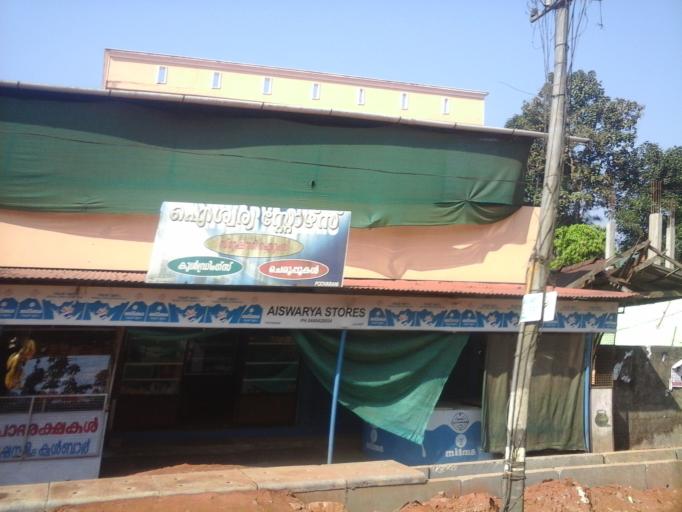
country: IN
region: Kerala
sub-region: Kottayam
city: Lalam
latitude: 9.6771
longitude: 76.6966
